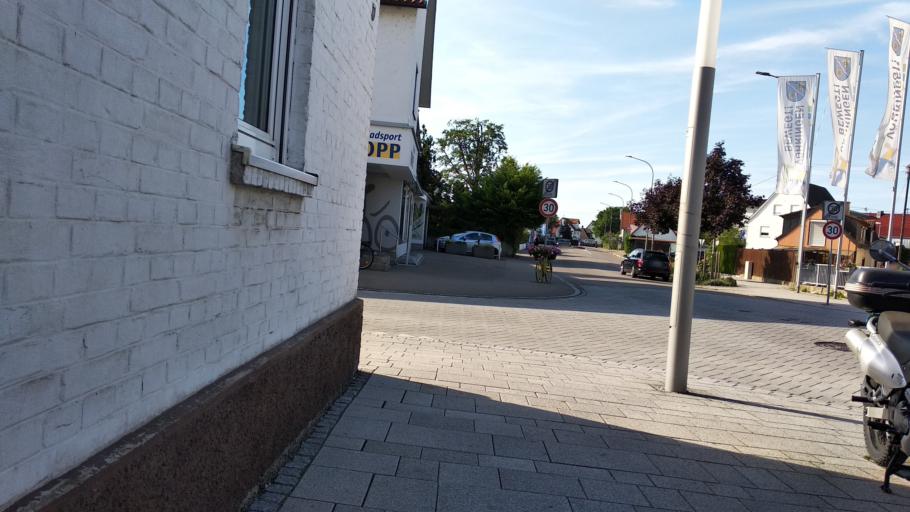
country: DE
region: Bavaria
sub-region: Swabia
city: Vohringen
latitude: 48.2791
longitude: 10.0780
